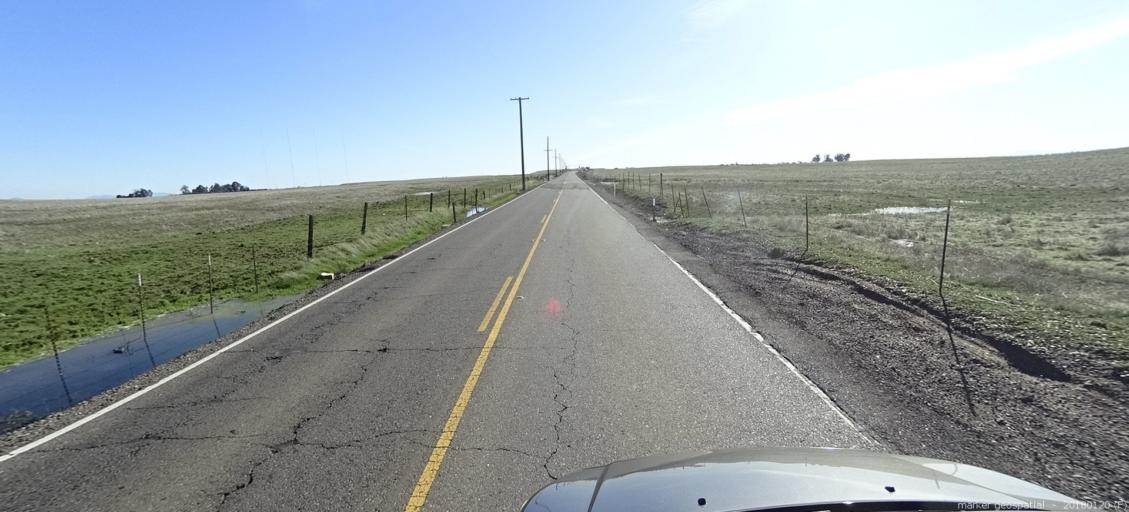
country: US
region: California
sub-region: Sacramento County
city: Gold River
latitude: 38.5650
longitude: -121.1873
